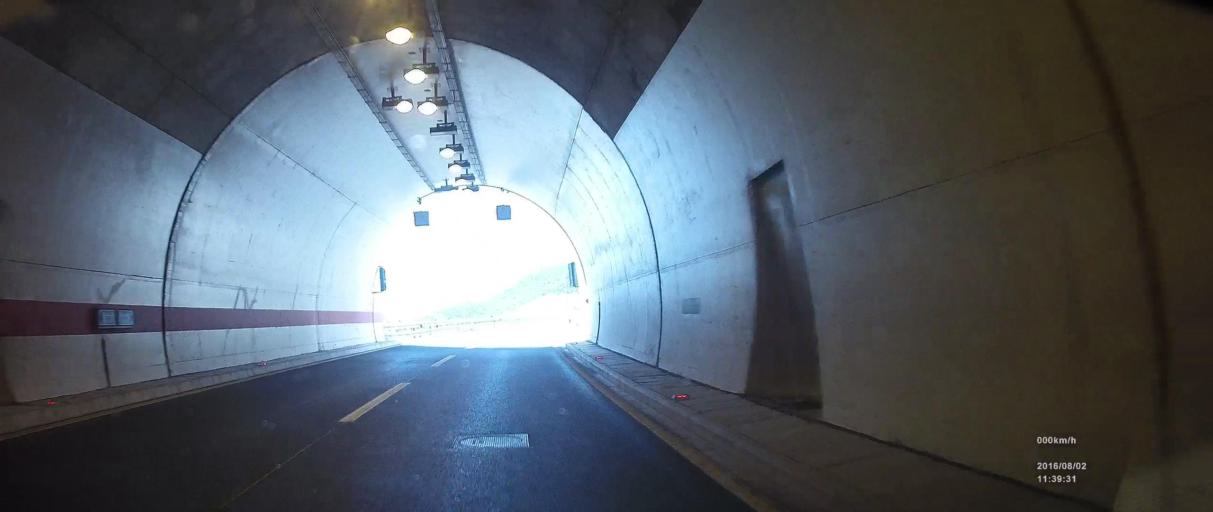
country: HR
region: Dubrovacko-Neretvanska
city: Komin
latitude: 43.0851
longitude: 17.4911
